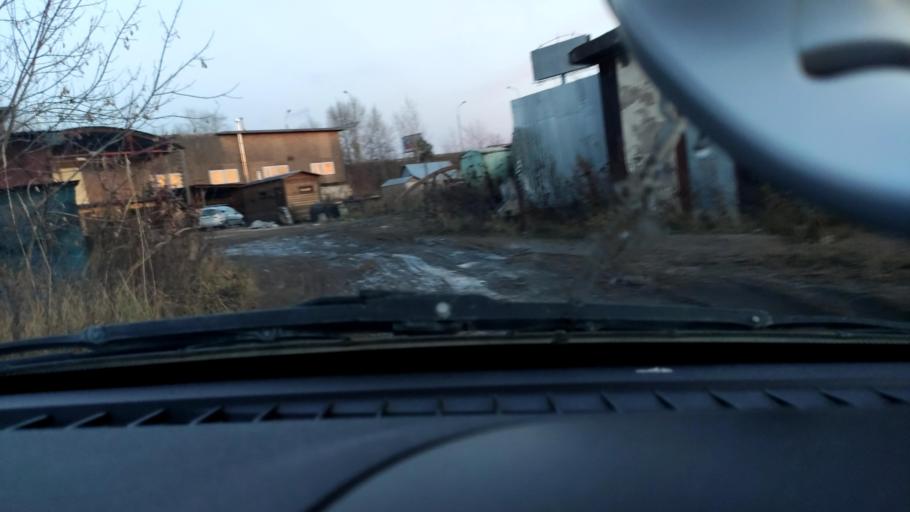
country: RU
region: Perm
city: Perm
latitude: 58.0247
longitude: 56.2175
